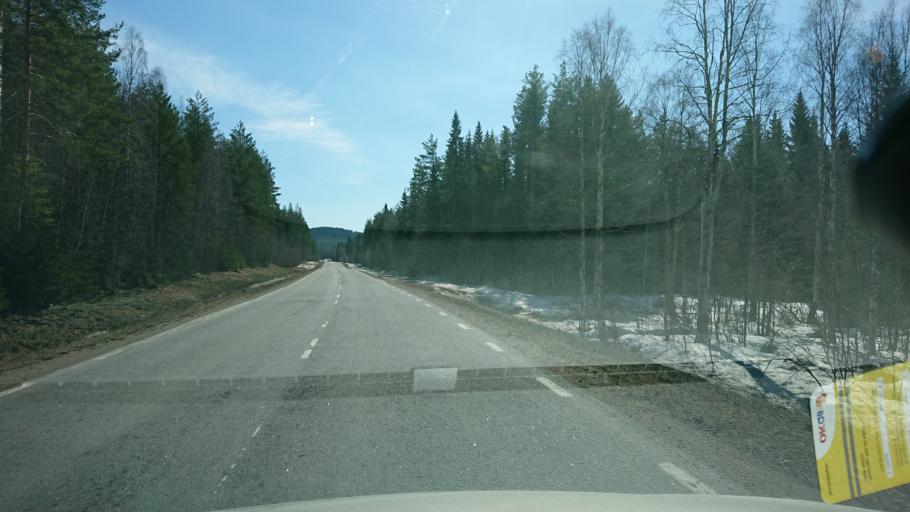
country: SE
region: Vaesternorrland
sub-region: Solleftea Kommun
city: As
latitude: 63.5779
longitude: 16.4374
